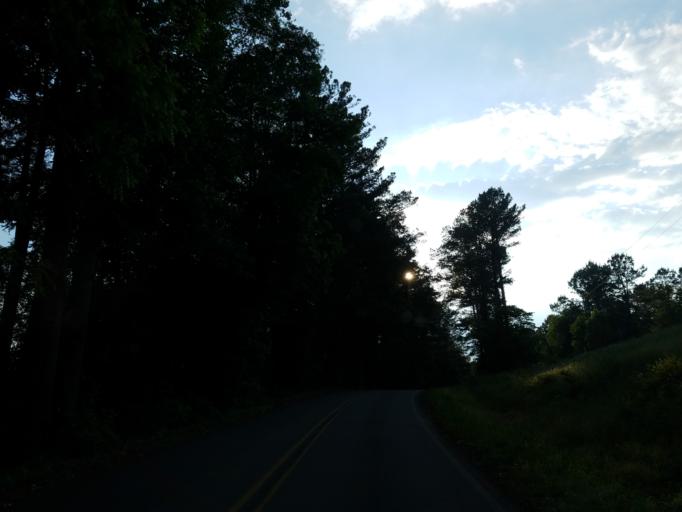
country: US
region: Georgia
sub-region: Cherokee County
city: Ball Ground
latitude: 34.2998
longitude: -84.3837
